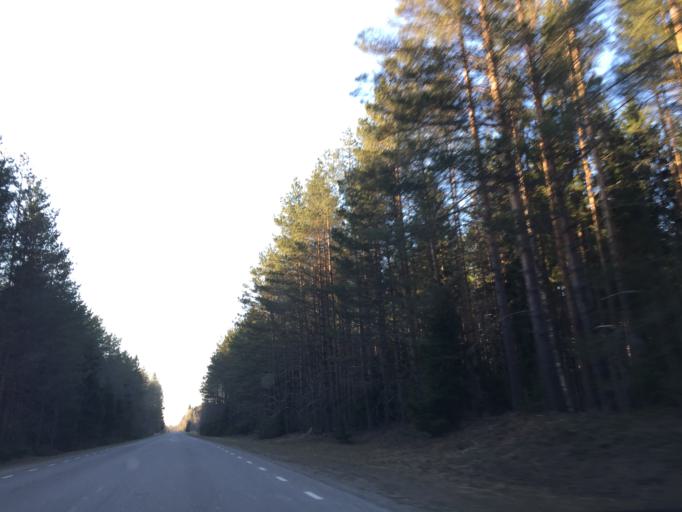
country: EE
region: Ida-Virumaa
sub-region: Toila vald
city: Voka
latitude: 59.1689
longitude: 27.5772
